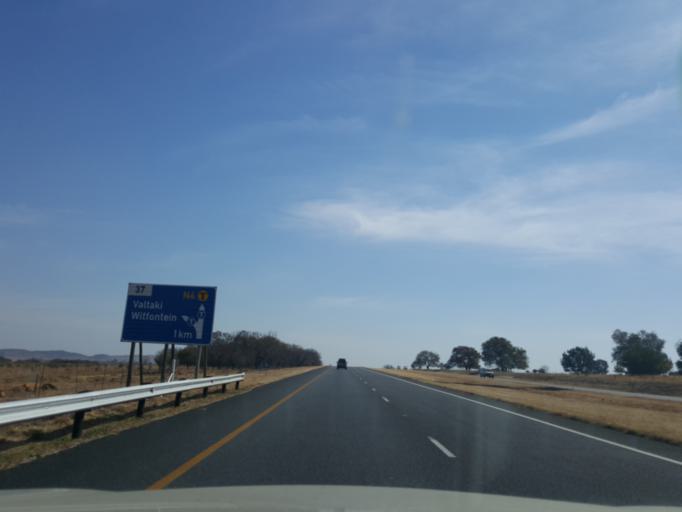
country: ZA
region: Gauteng
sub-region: City of Tshwane Metropolitan Municipality
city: Bronkhorstspruit
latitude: -25.7996
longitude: 28.6343
